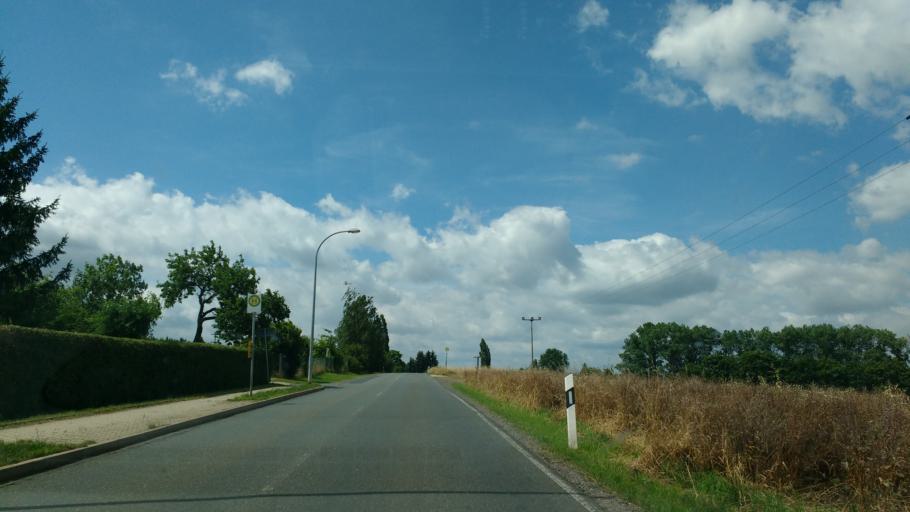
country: DE
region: Saxony-Anhalt
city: Zeitz
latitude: 51.0350
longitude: 12.1320
